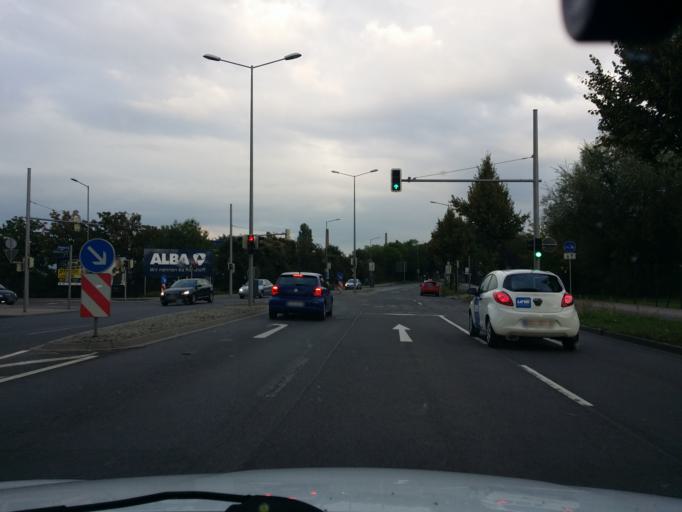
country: DE
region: Saxony
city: Leipzig
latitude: 51.3425
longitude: 12.3032
